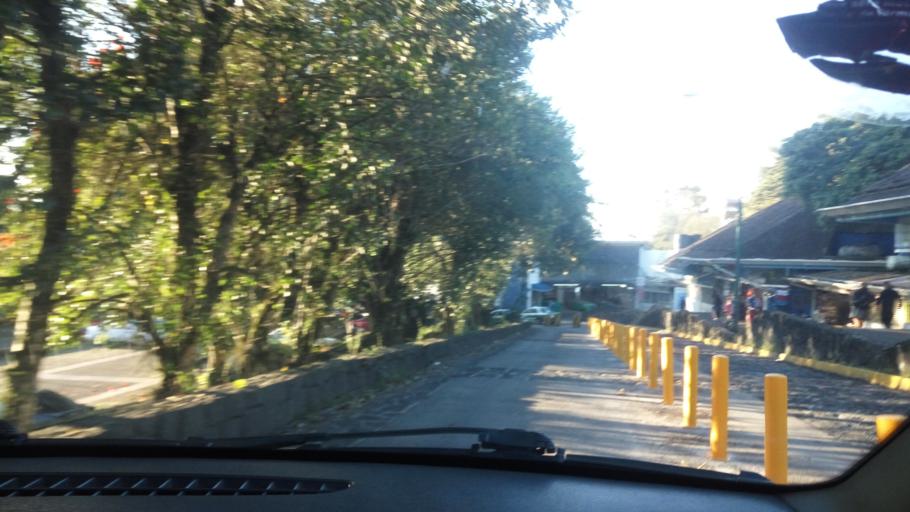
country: MX
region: Veracruz
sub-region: Xalapa
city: Xalapa de Enriquez
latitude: 19.5266
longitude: -96.9037
